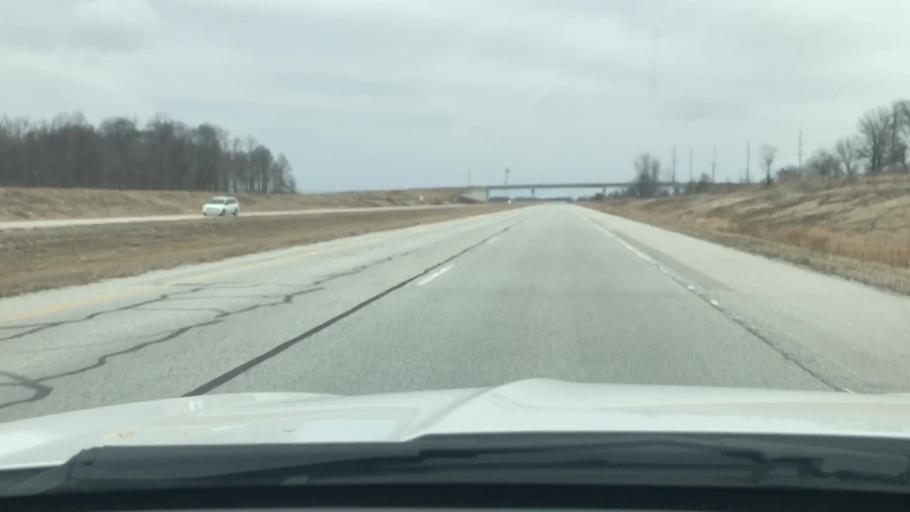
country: US
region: Indiana
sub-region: Cass County
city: Georgetown
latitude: 40.6590
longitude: -86.5417
